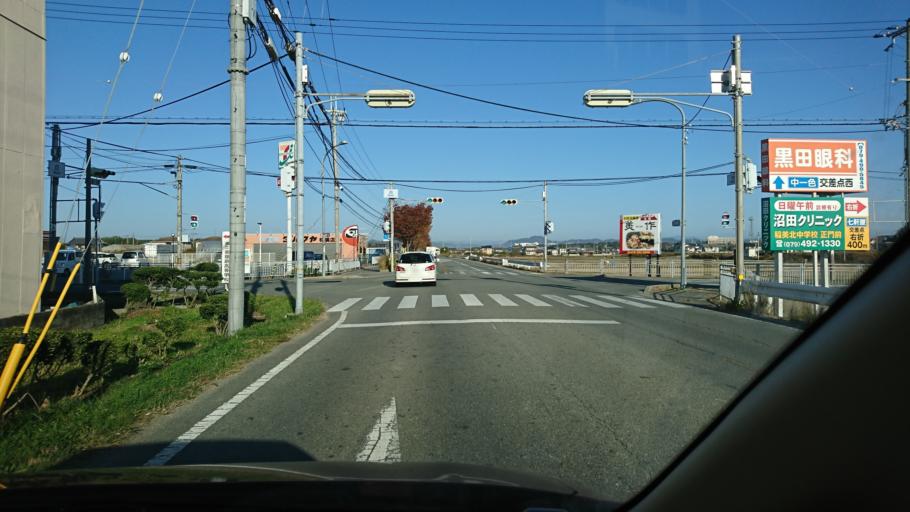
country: JP
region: Hyogo
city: Kakogawacho-honmachi
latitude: 34.7532
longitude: 134.8927
